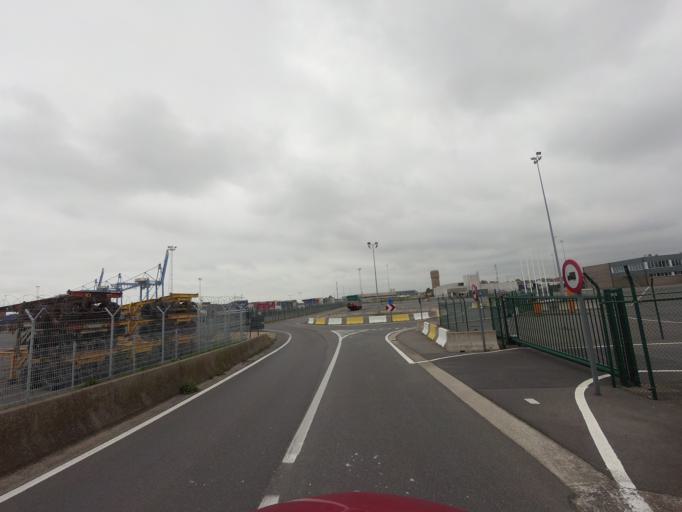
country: BE
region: Flanders
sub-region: Provincie West-Vlaanderen
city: Zeebrugge
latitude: 51.3289
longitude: 3.1884
